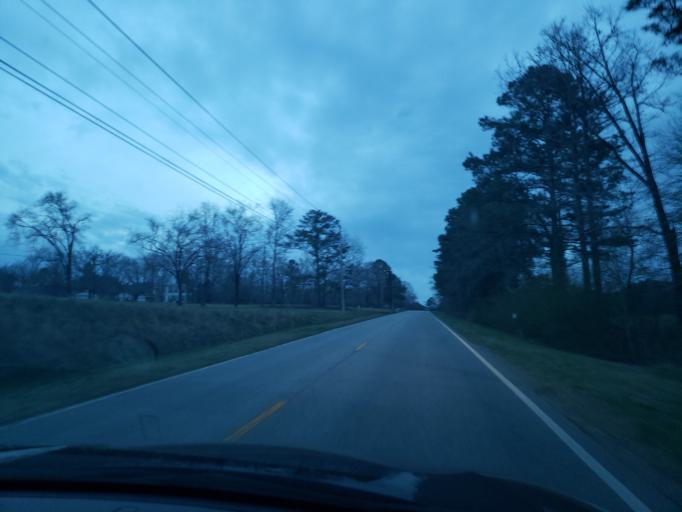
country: US
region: Alabama
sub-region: Lee County
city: Auburn
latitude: 32.6371
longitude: -85.4652
